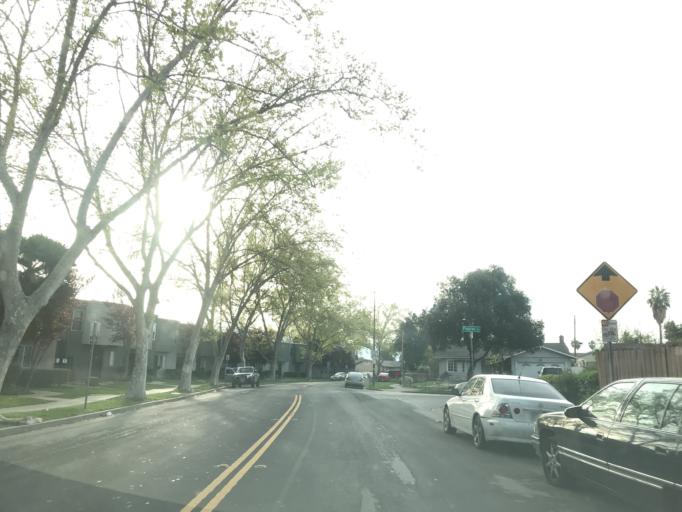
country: US
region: California
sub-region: Santa Clara County
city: Alum Rock
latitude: 37.3445
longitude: -121.8264
